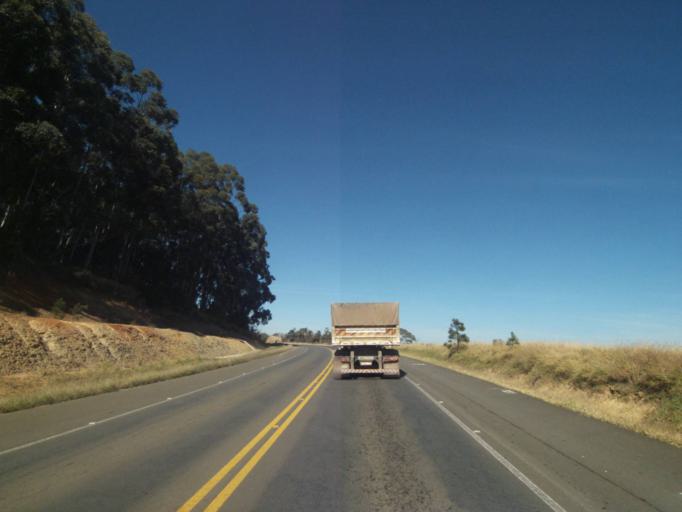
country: BR
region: Parana
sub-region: Tibagi
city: Tibagi
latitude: -24.7623
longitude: -50.4701
